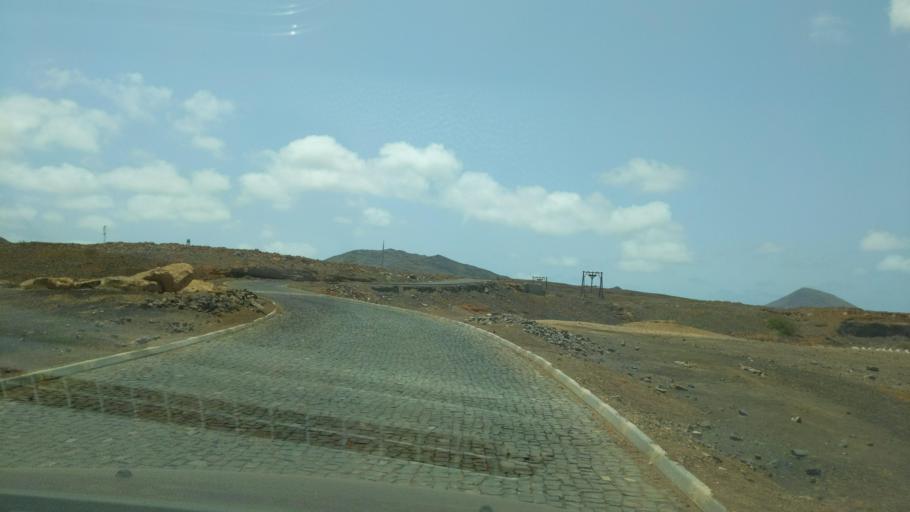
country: CV
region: Sal
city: Espargos
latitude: 16.7642
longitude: -22.8927
